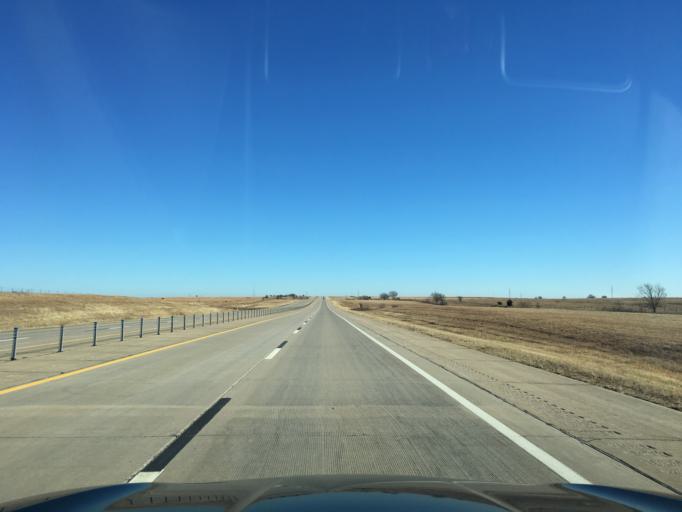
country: US
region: Oklahoma
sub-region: Noble County
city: Perry
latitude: 36.3920
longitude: -97.1363
